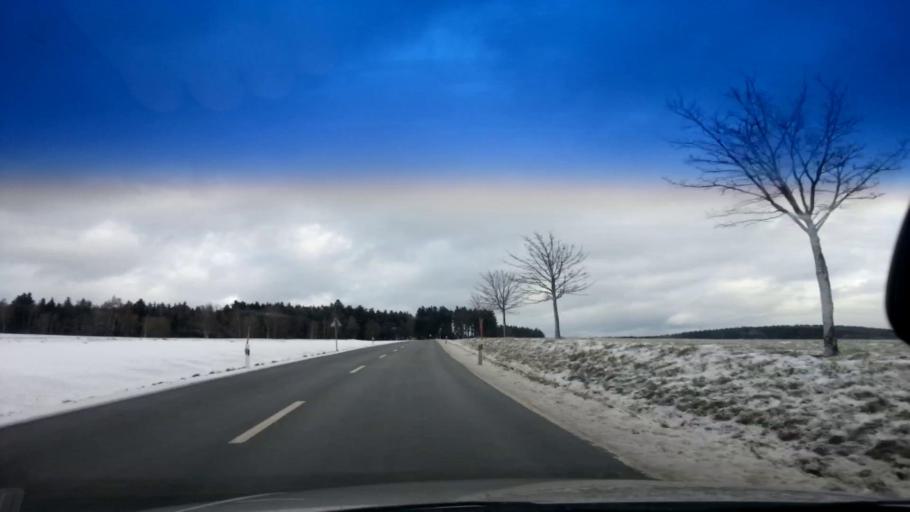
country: DE
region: Bavaria
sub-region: Upper Franconia
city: Grub
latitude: 50.1313
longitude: 11.9239
